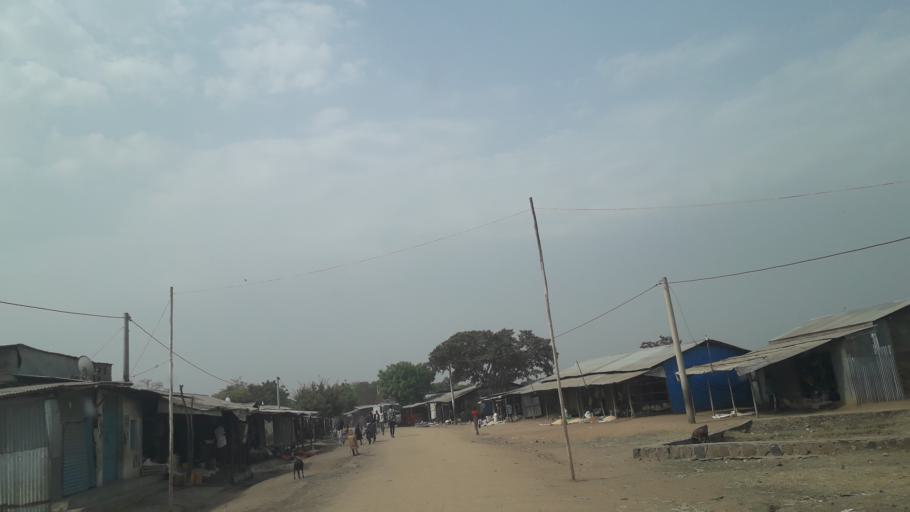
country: ET
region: Gambela
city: Gambela
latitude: 8.3035
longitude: 33.6841
